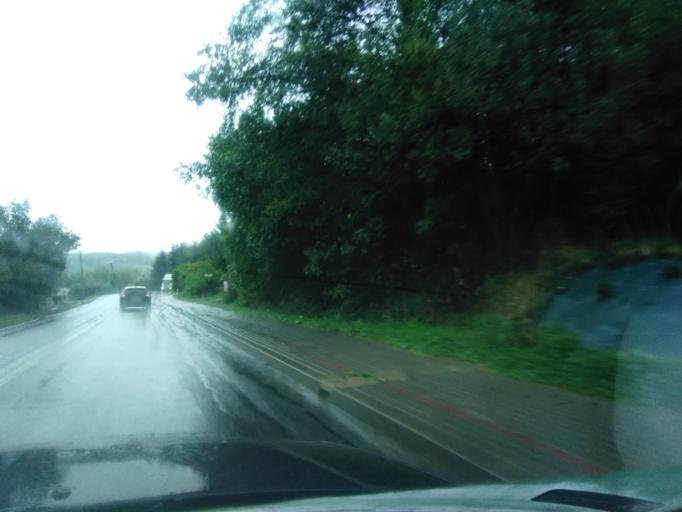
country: PL
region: Subcarpathian Voivodeship
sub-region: Powiat ropczycko-sedziszowski
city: Niedzwiada
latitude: 50.0201
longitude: 21.5469
